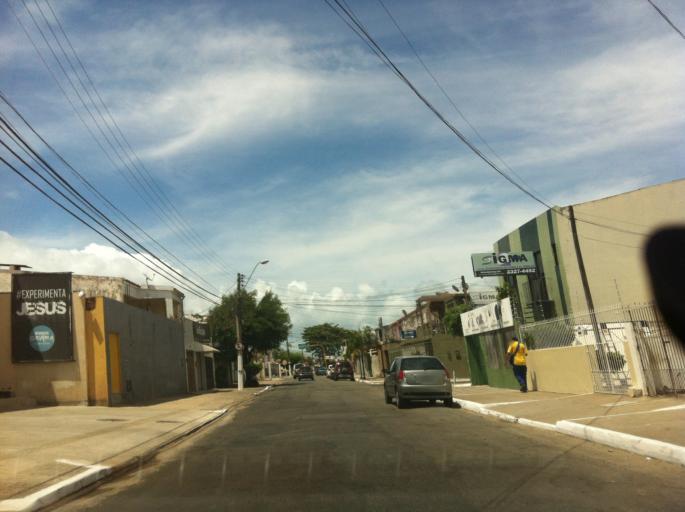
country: BR
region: Alagoas
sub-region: Maceio
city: Maceio
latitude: -9.6675
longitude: -35.7152
